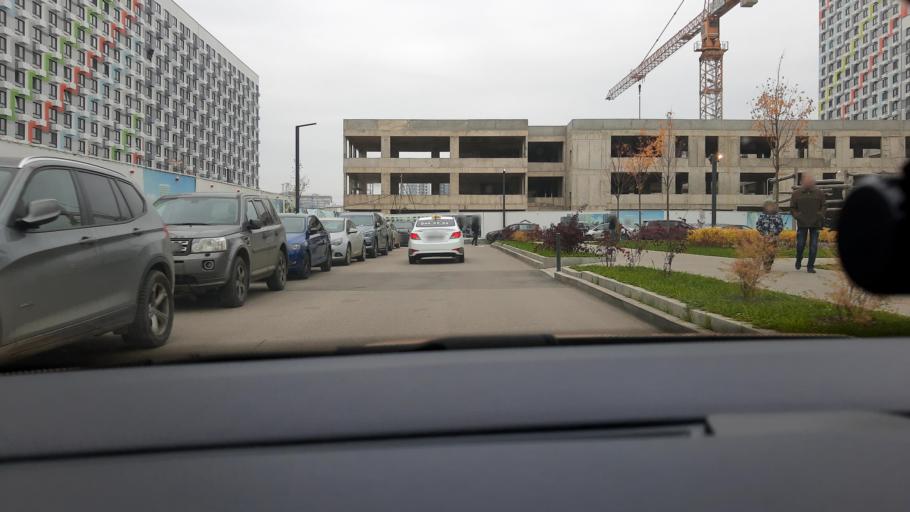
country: RU
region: Moscow
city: Otradnoye
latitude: 55.8743
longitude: 37.6015
